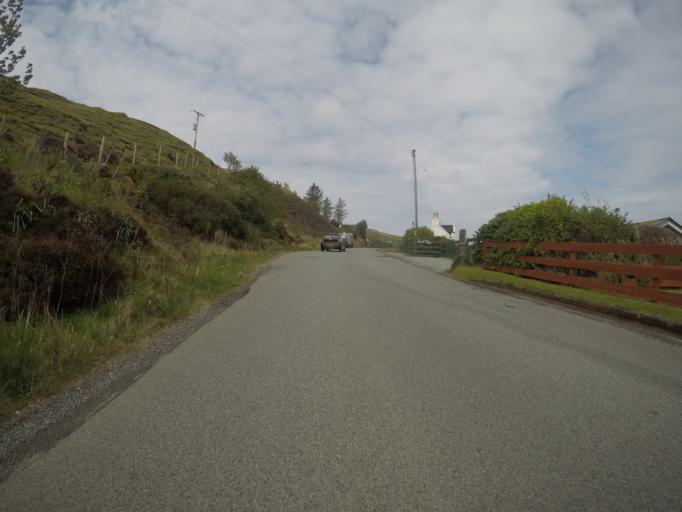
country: GB
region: Scotland
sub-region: Highland
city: Portree
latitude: 57.6370
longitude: -6.2411
